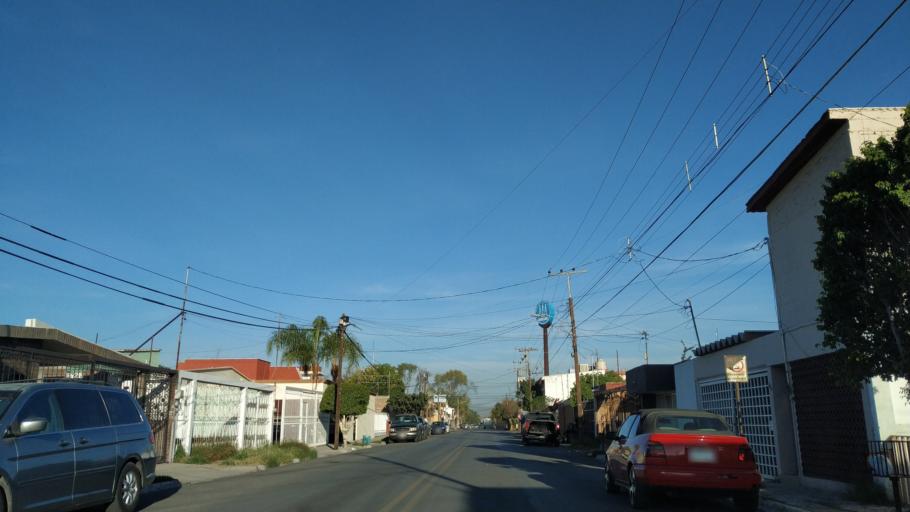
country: MX
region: Coahuila
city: Torreon
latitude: 25.5512
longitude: -103.4492
